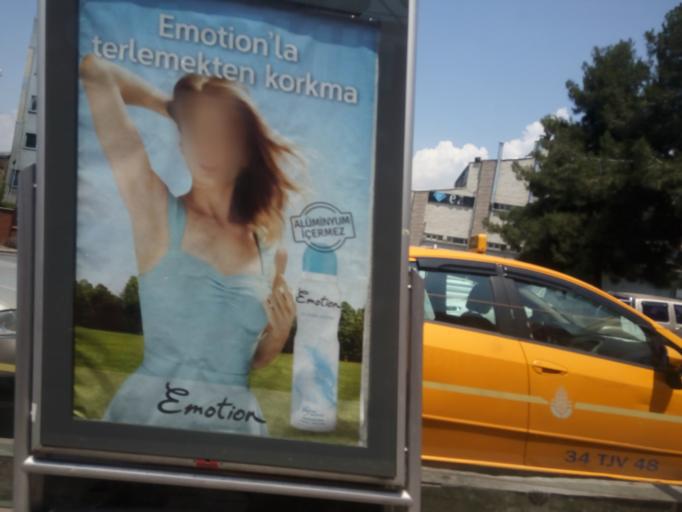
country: TR
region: Istanbul
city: Zeytinburnu
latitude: 41.0035
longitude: 28.8999
